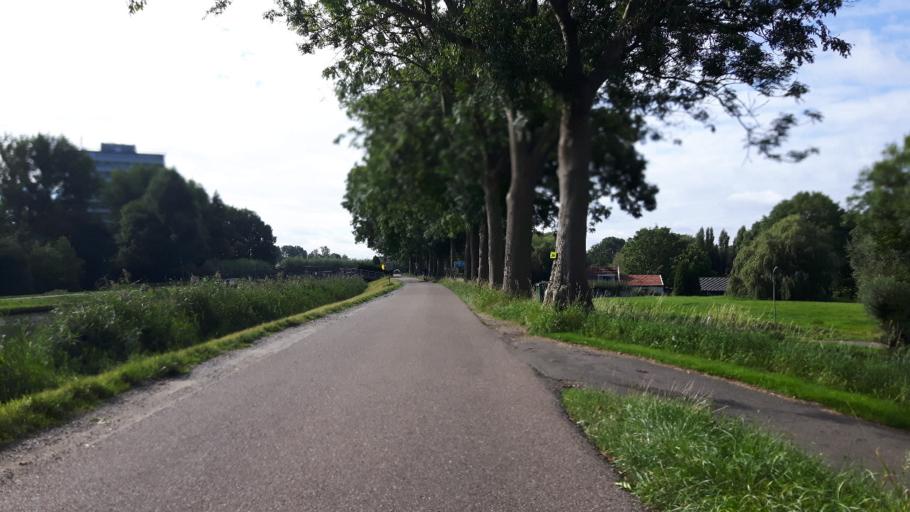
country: NL
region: North Holland
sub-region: Gemeente Purmerend
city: Purmerend
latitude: 52.5188
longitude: 4.9544
